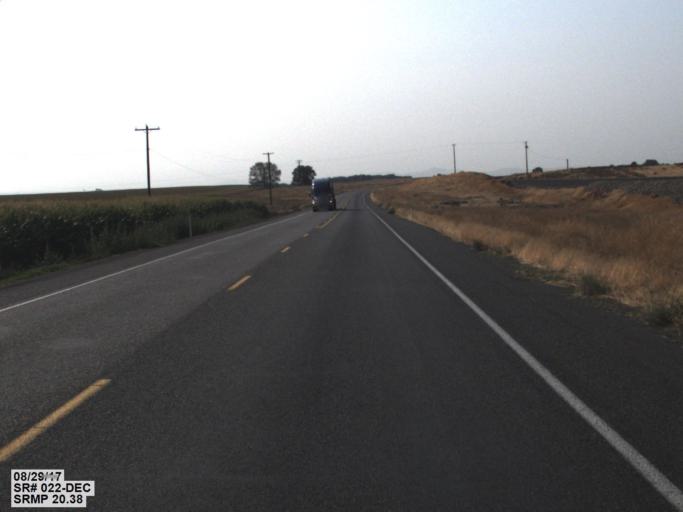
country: US
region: Washington
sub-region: Yakima County
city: Mabton
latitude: 46.2248
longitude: -120.0535
